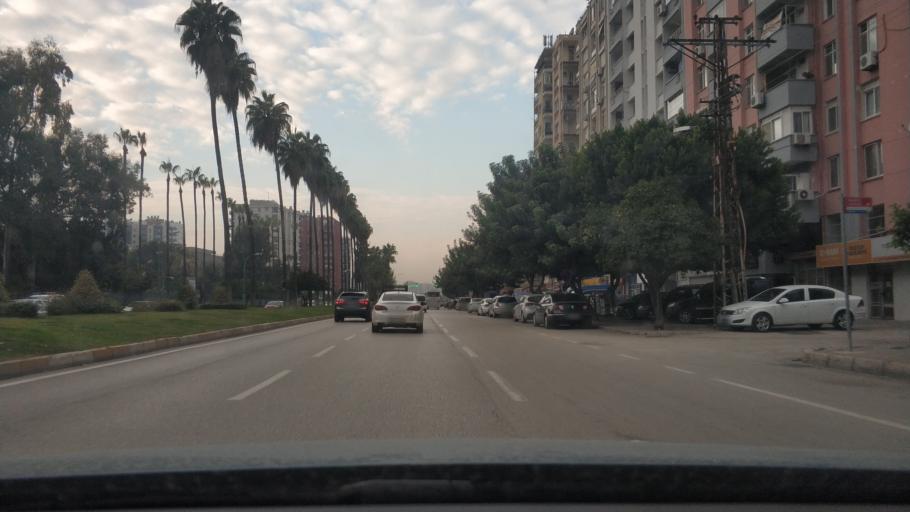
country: TR
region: Adana
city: Adana
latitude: 37.0002
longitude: 35.3157
